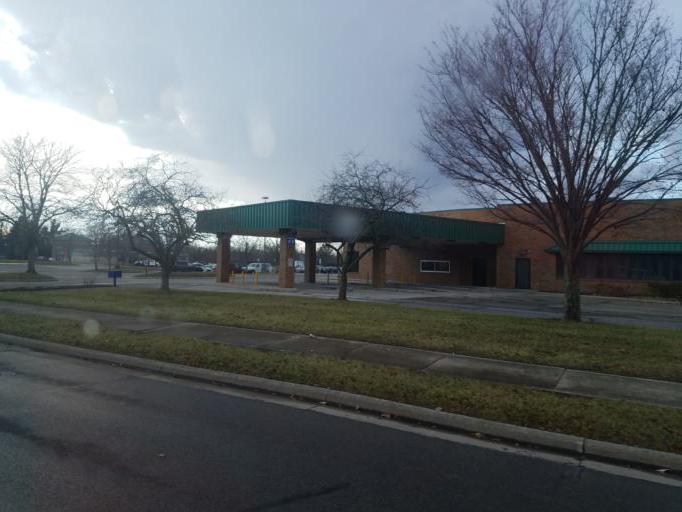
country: US
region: Ohio
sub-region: Delaware County
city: Delaware
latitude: 40.3090
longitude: -83.0945
